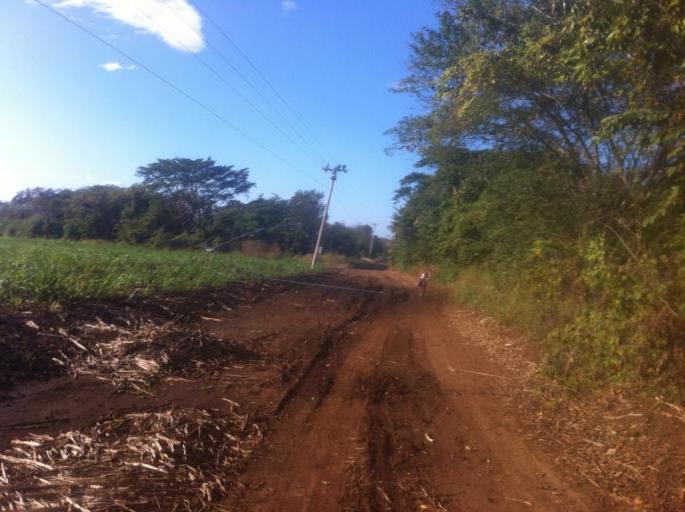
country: NI
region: Managua
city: Masachapa
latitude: 11.8675
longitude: -86.5624
